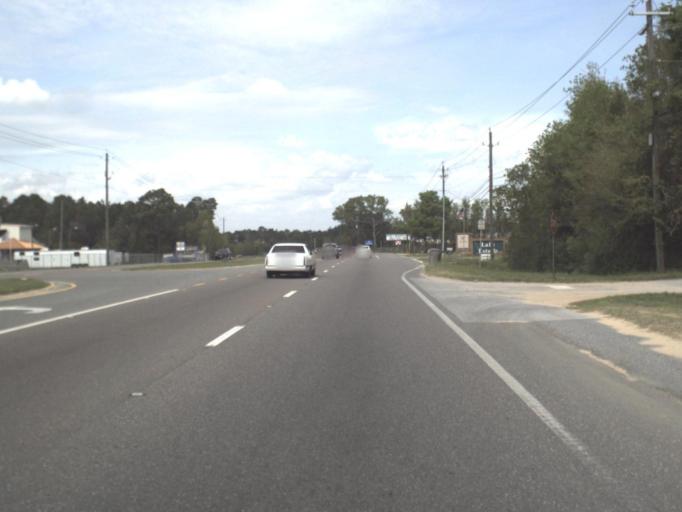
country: US
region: Florida
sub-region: Escambia County
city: Ensley
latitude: 30.5018
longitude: -87.3057
